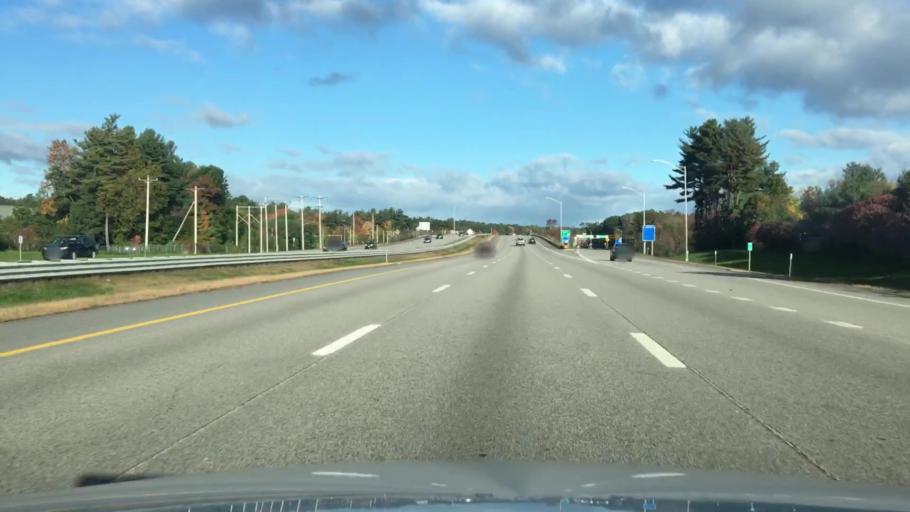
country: US
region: Maine
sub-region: York County
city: South Eliot
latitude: 43.0875
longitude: -70.7982
